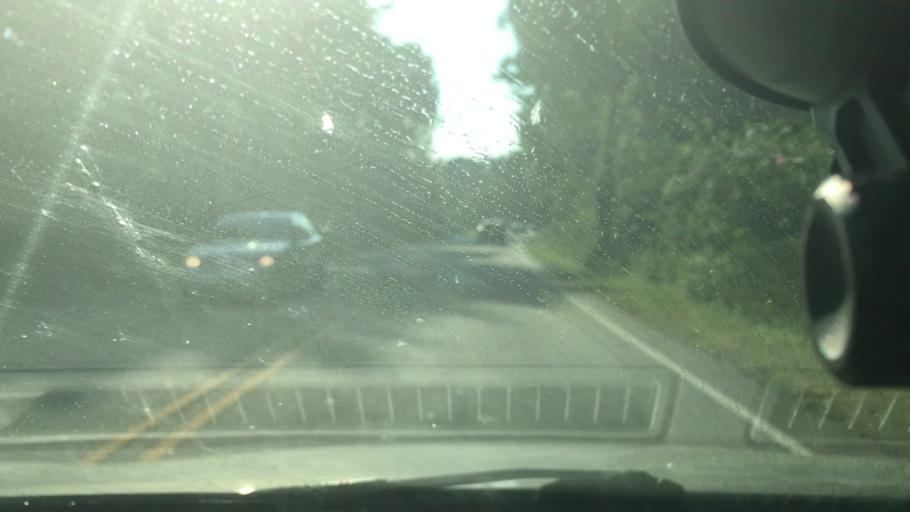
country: US
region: North Carolina
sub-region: Wake County
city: Apex
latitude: 35.7277
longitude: -78.8554
